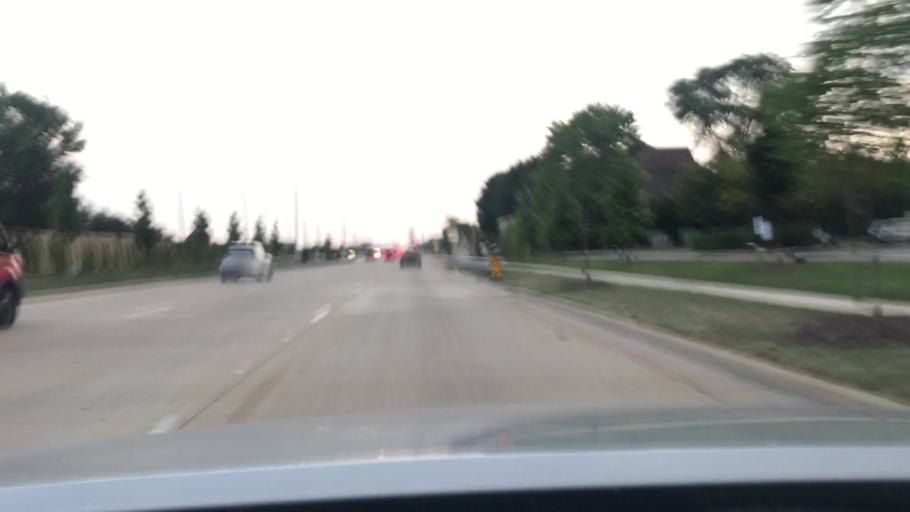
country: US
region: Illinois
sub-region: DuPage County
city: Warrenville
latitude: 41.7862
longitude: -88.2058
